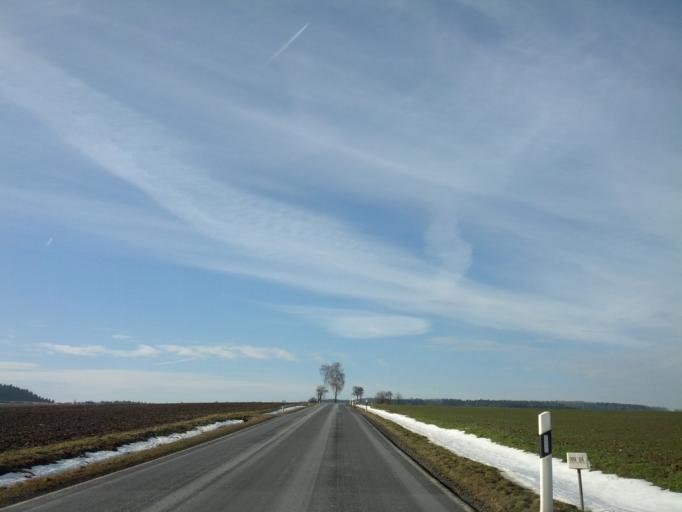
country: DE
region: Thuringia
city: Friedrichswerth
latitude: 51.0463
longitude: 10.5279
